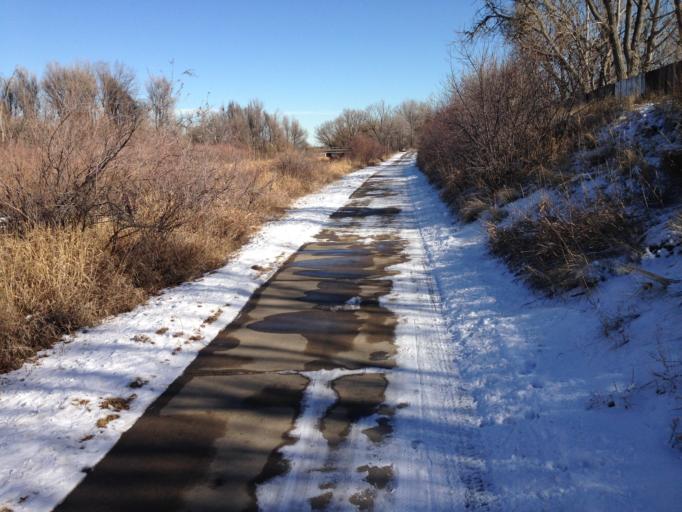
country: US
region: Colorado
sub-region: Adams County
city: Berkley
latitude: 39.7965
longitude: -105.0463
